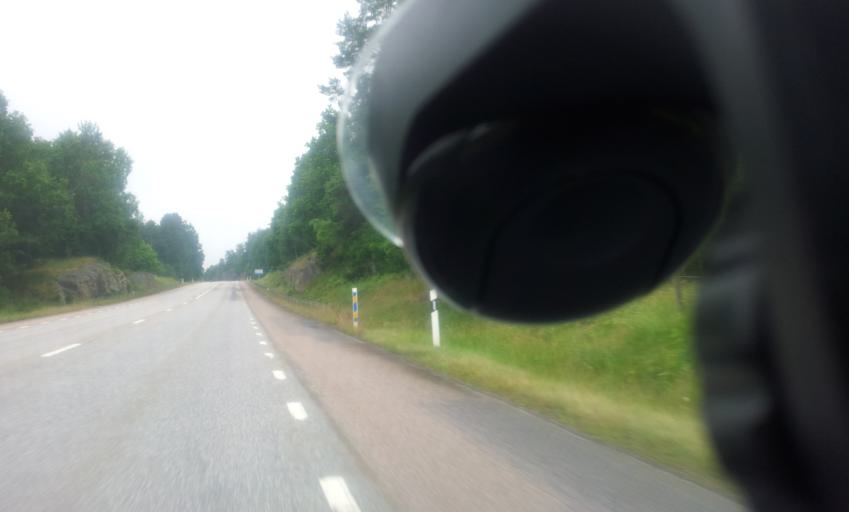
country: SE
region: Kalmar
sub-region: Vasterviks Kommun
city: Ankarsrum
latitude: 57.6726
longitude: 16.4427
